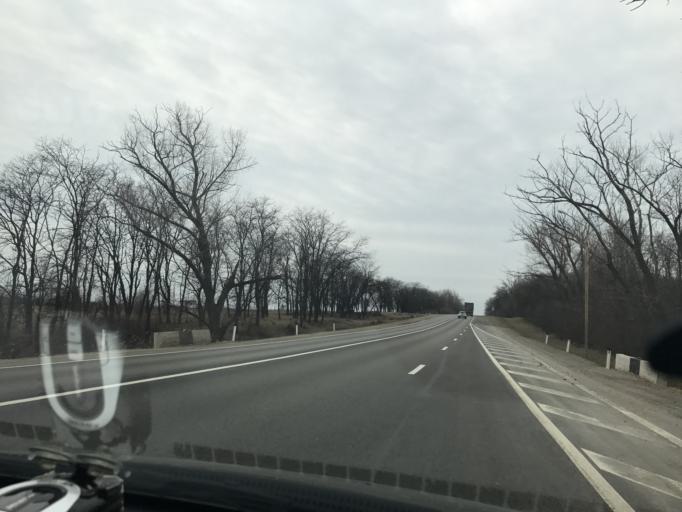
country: RU
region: Krasnodarskiy
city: Mirskoy
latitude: 45.6712
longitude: 40.3246
